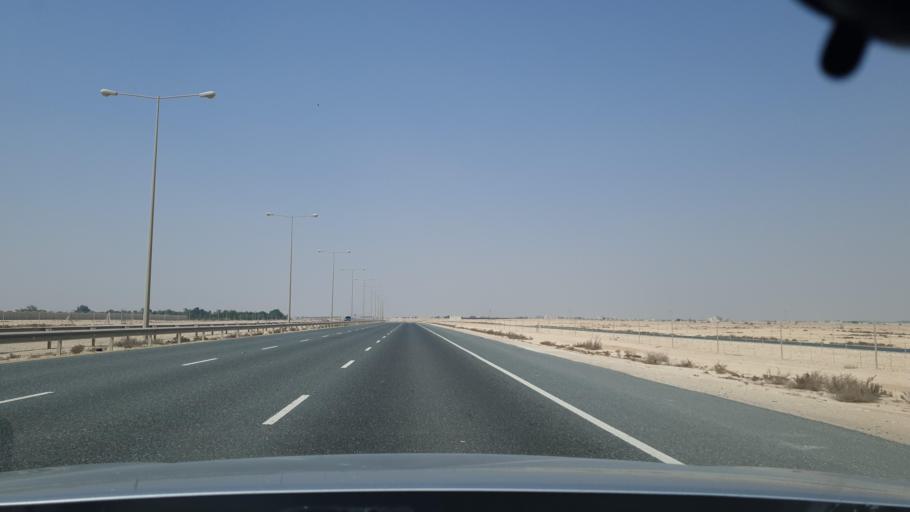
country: QA
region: Al Khawr
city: Al Khawr
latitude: 25.7717
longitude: 51.4134
